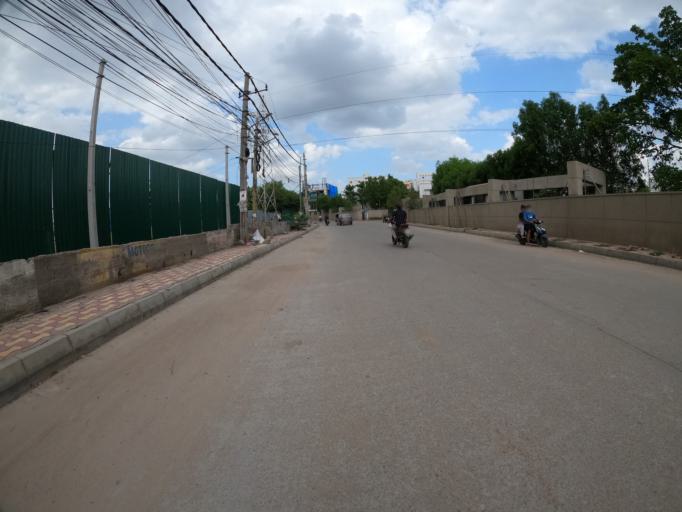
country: IN
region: Telangana
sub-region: Hyderabad
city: Hyderabad
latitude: 17.4070
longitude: 78.3852
